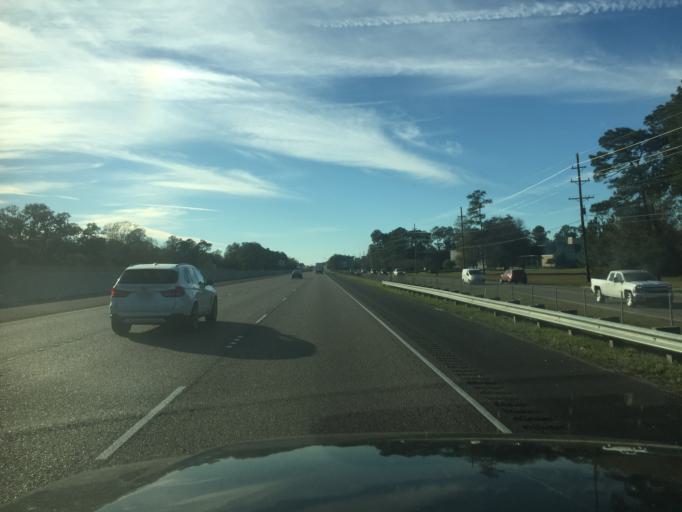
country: US
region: Louisiana
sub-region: Saint Tammany Parish
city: Slidell
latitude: 30.3102
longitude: -89.7580
